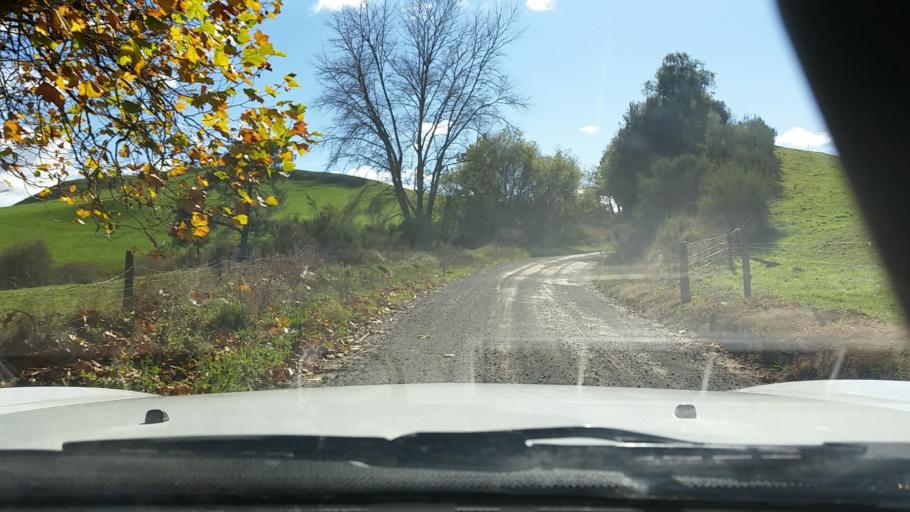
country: NZ
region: Waikato
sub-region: South Waikato District
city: Tokoroa
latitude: -38.3762
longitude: 176.0859
